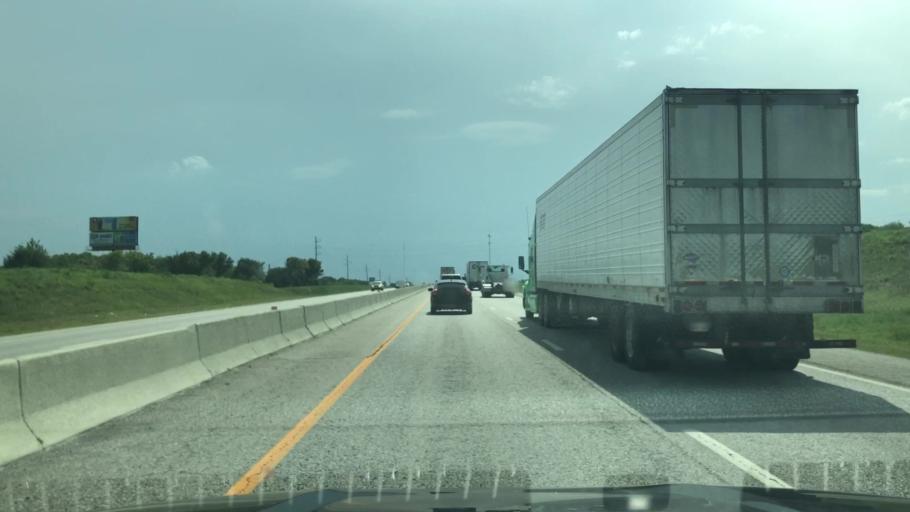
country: US
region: Oklahoma
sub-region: Craig County
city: Vinita
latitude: 36.6467
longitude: -95.1142
